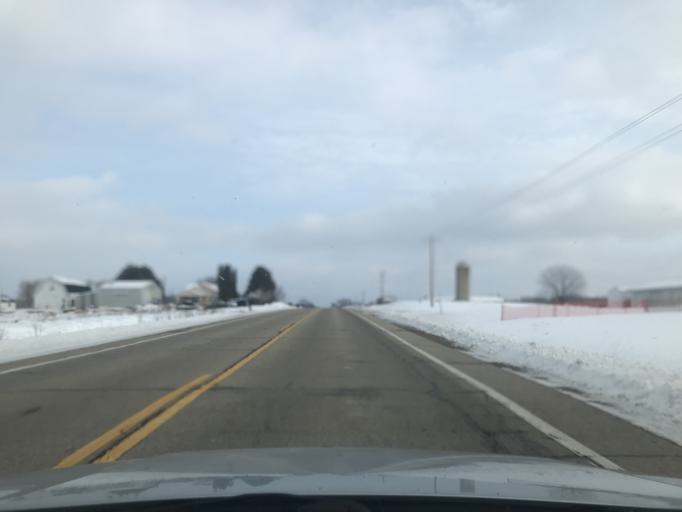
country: US
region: Wisconsin
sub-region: Oconto County
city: Oconto
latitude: 44.8933
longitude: -87.9872
